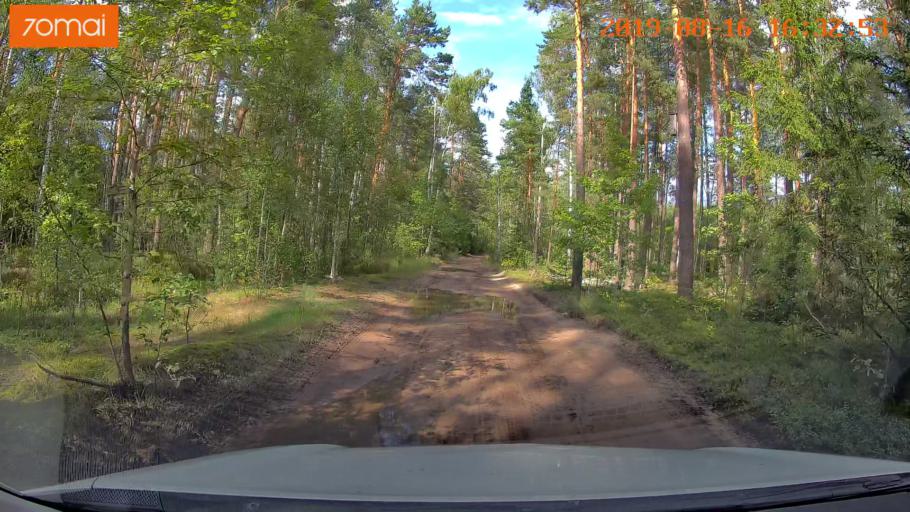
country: BY
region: Mogilev
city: Asipovichy
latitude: 53.2278
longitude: 28.7743
